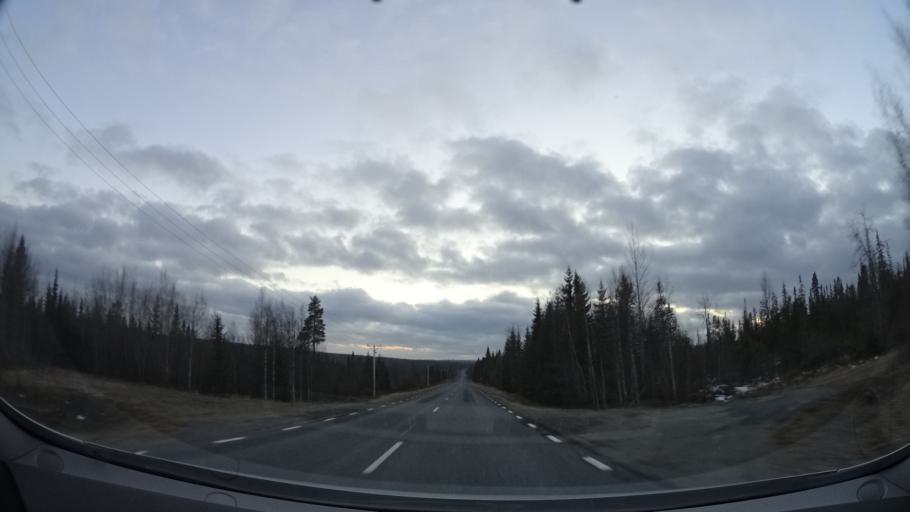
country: SE
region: Vaesterbotten
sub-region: Lycksele Kommun
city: Soderfors
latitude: 64.3810
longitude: 17.9873
